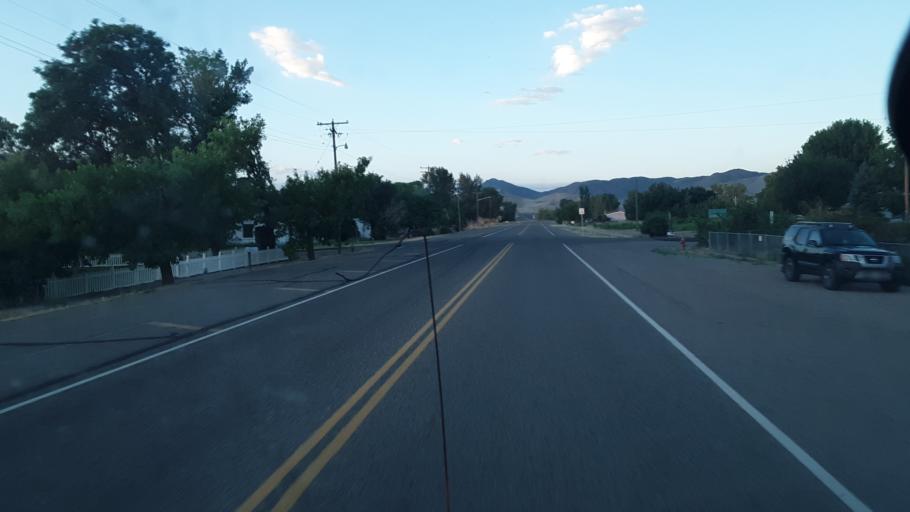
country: US
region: Utah
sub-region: Sevier County
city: Monroe
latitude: 38.6233
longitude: -112.2184
